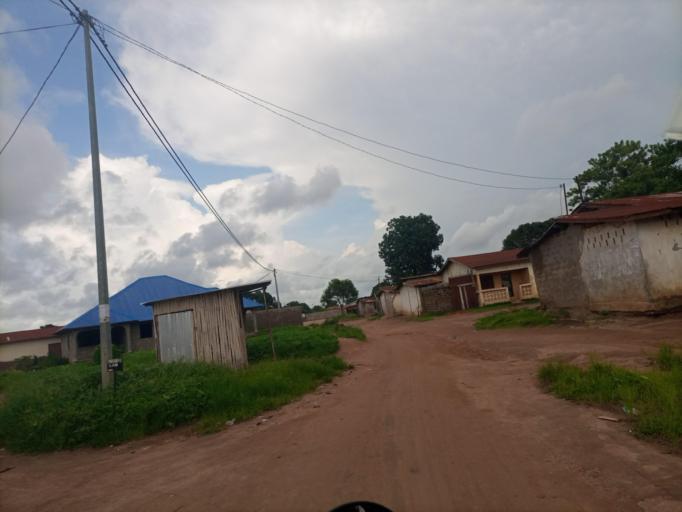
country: SL
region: Northern Province
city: Masoyila
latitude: 8.6082
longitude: -13.1759
